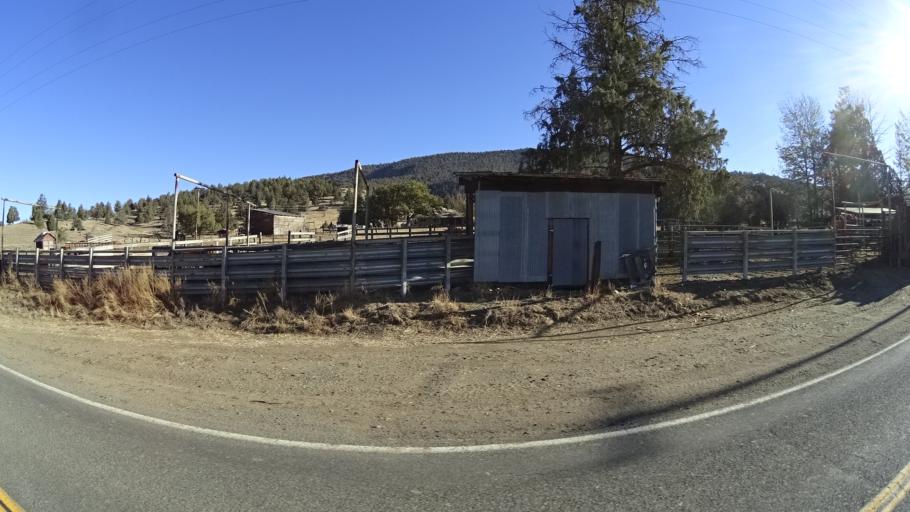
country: US
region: California
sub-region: Siskiyou County
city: Yreka
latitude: 41.5080
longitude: -122.8392
